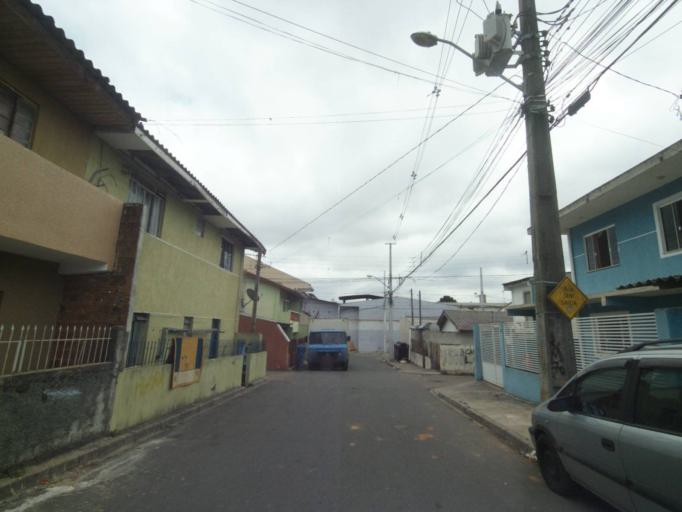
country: BR
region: Parana
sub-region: Sao Jose Dos Pinhais
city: Sao Jose dos Pinhais
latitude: -25.5352
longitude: -49.2672
